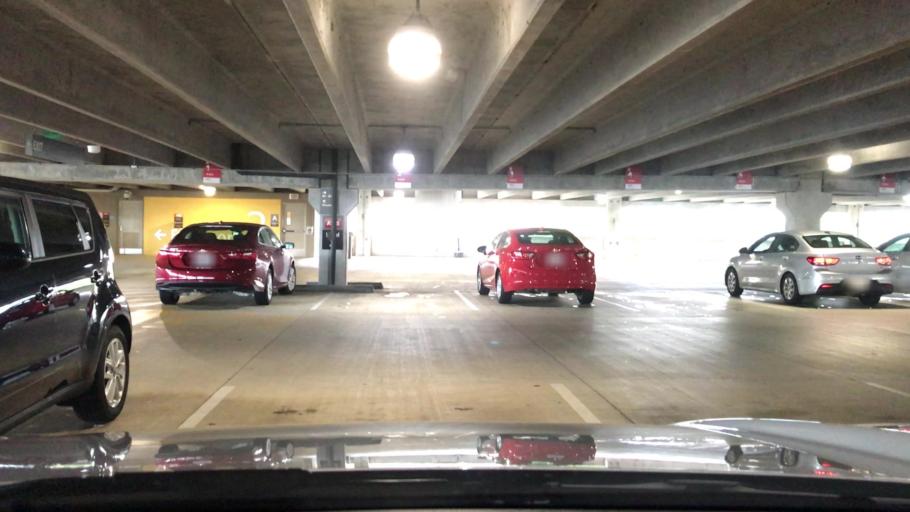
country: US
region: Louisiana
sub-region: East Baton Rouge Parish
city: Brownsfield
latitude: 30.5342
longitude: -91.1576
